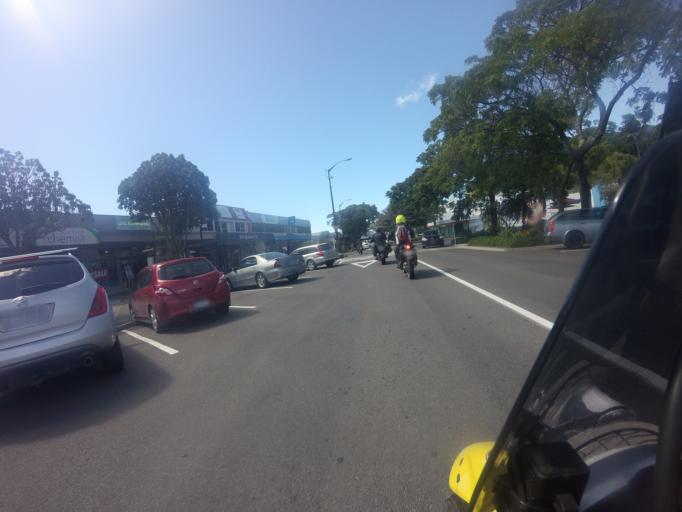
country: NZ
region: Bay of Plenty
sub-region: Whakatane District
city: Whakatane
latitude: -37.9523
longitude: 176.9932
